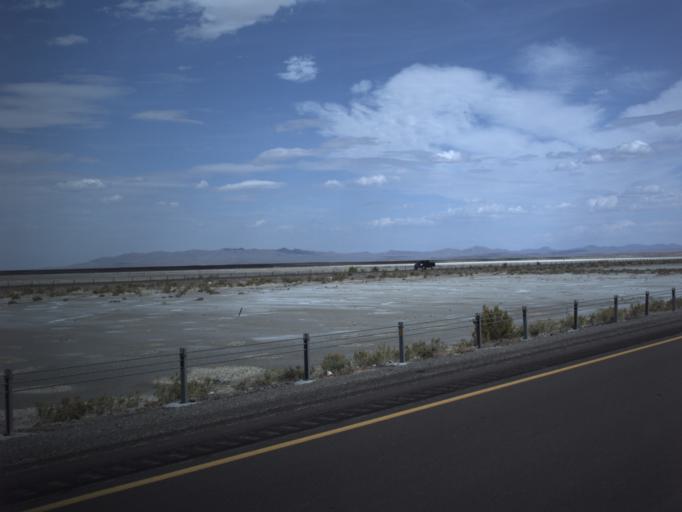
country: US
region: Utah
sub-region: Tooele County
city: Wendover
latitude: 40.7278
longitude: -113.3542
